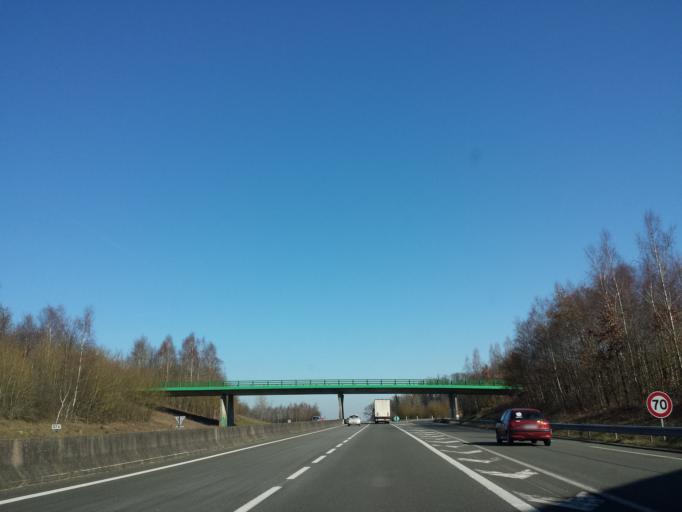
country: FR
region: Picardie
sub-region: Departement de l'Oise
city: Allonne
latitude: 49.3961
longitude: 2.1214
